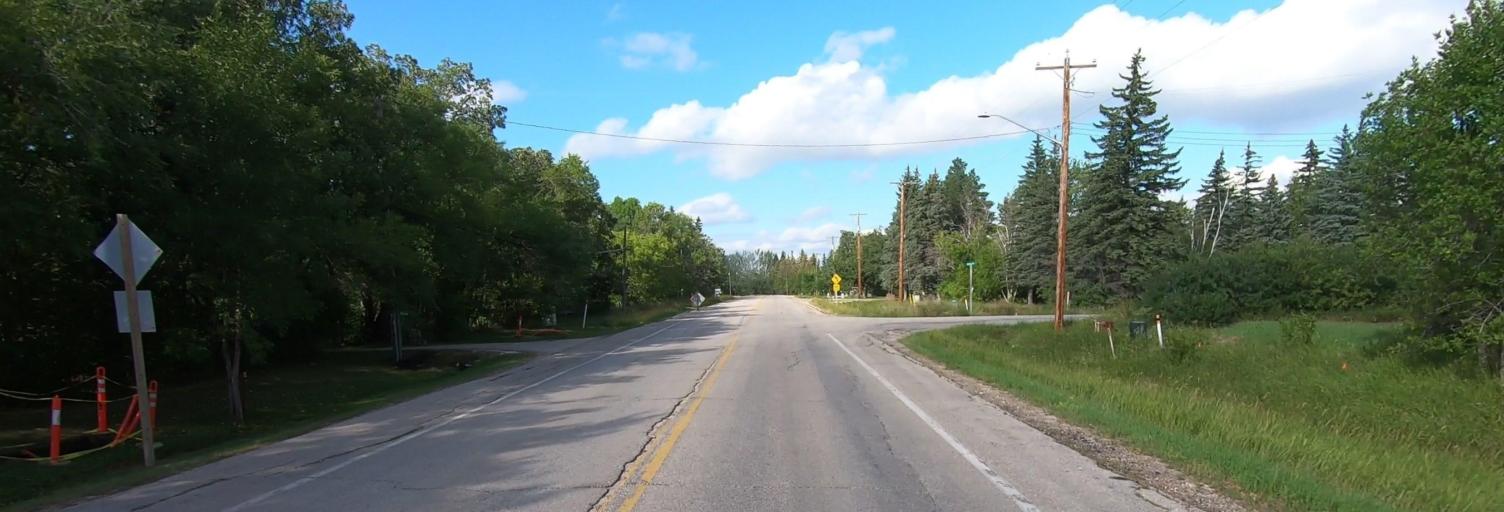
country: CA
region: Manitoba
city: Selkirk
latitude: 50.0390
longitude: -96.9851
